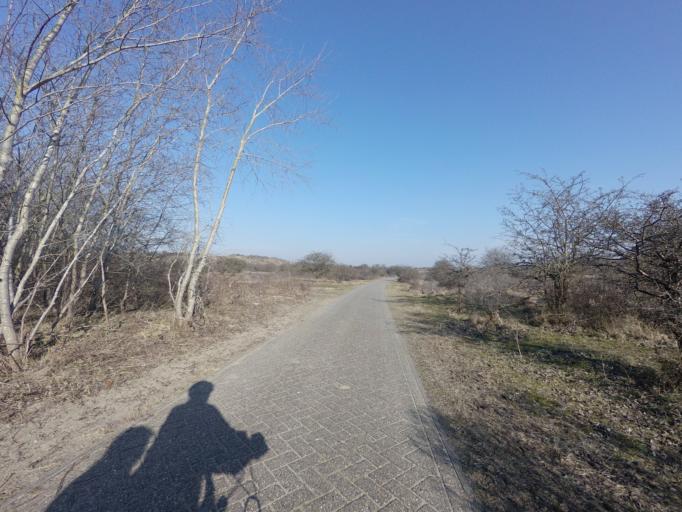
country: NL
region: North Holland
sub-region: Gemeente Bloemendaal
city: Bloemendaal
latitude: 52.4252
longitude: 4.5782
